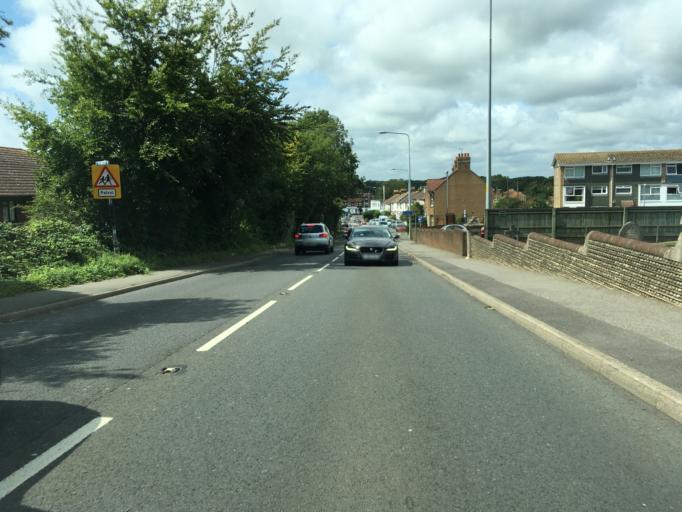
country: GB
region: England
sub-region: East Sussex
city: Bexhill-on-Sea
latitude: 50.8455
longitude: 0.4371
